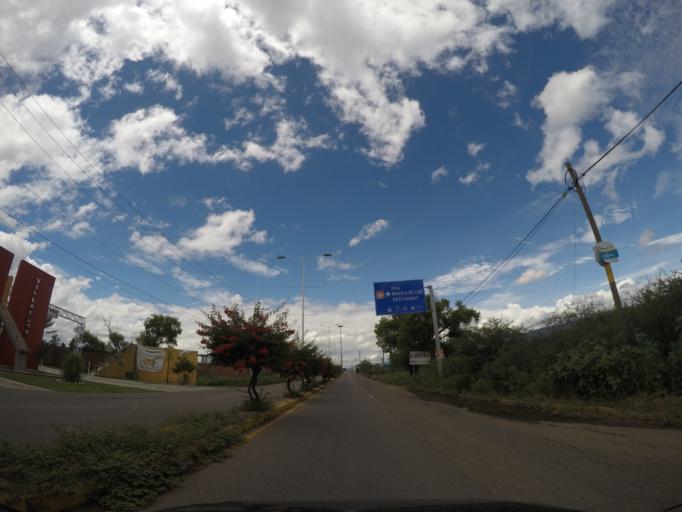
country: MX
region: Oaxaca
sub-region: Santa Cruz Xoxocotlan
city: San Isidro Monjas
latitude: 16.9986
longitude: -96.7410
